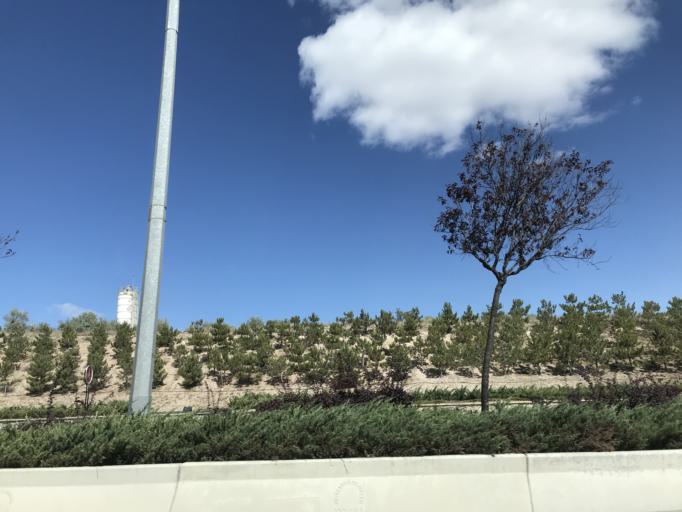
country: TR
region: Ankara
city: Batikent
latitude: 39.9253
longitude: 32.7508
